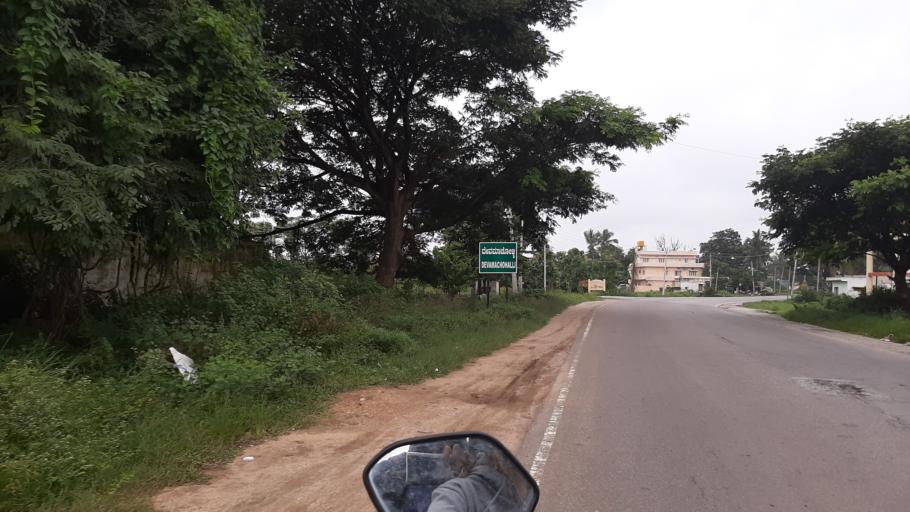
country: IN
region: Karnataka
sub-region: Bangalore Rural
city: Nelamangala
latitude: 12.9653
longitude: 77.3817
